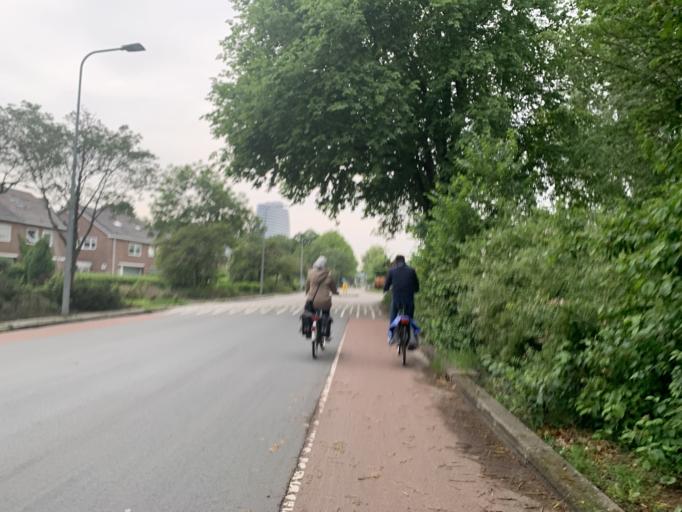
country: NL
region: Groningen
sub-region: Gemeente Groningen
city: Oosterpark
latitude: 53.2031
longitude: 6.5873
